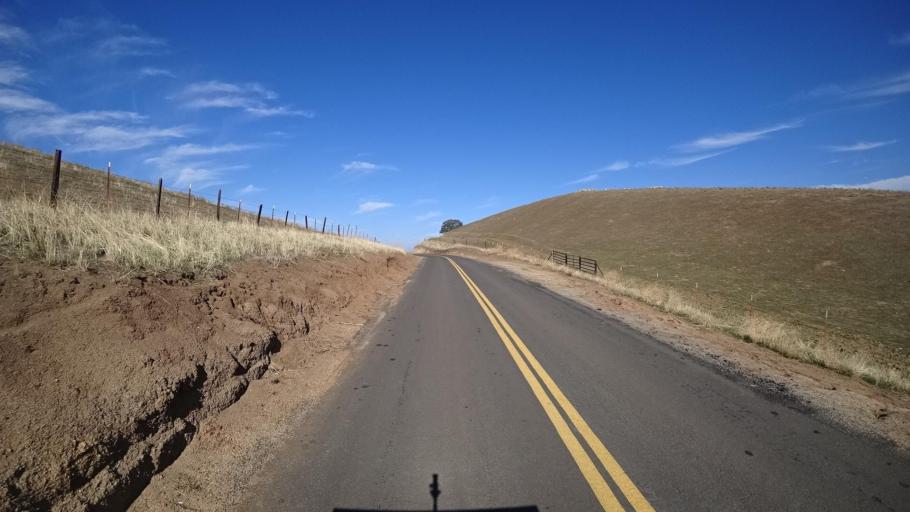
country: US
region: California
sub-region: Tulare County
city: Richgrove
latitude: 35.6867
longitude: -118.8800
